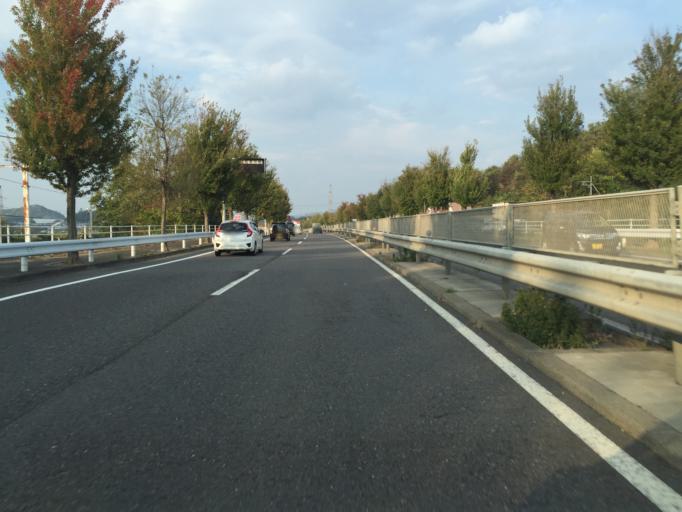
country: JP
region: Fukushima
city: Nihommatsu
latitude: 37.6414
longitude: 140.4852
